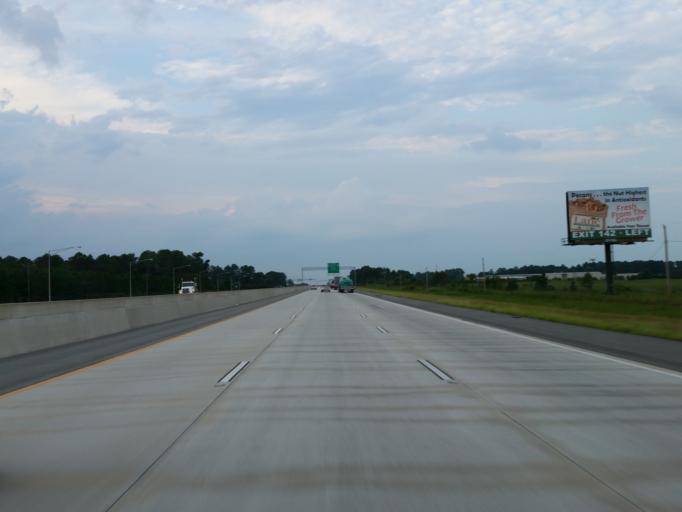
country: US
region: Georgia
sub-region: Cook County
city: Sparks
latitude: 31.2560
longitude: -83.4691
